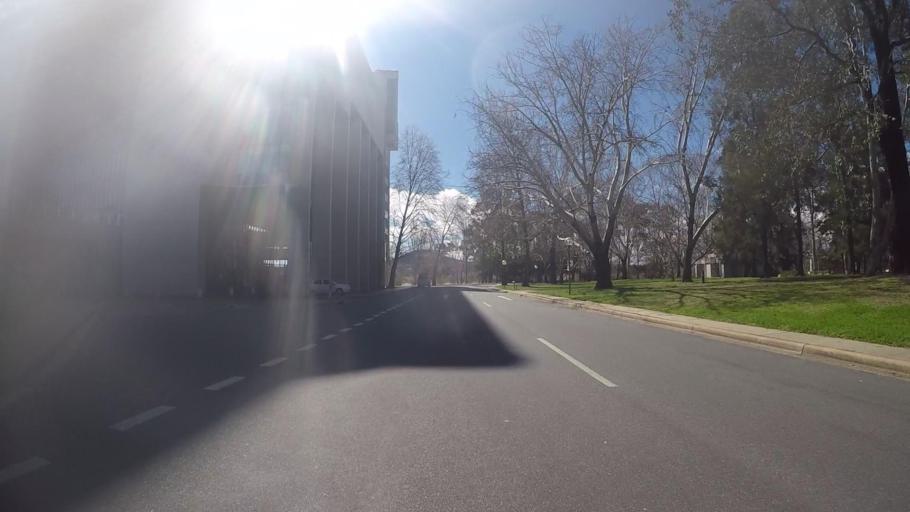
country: AU
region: Australian Capital Territory
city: Forrest
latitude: -35.2997
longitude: 149.1357
